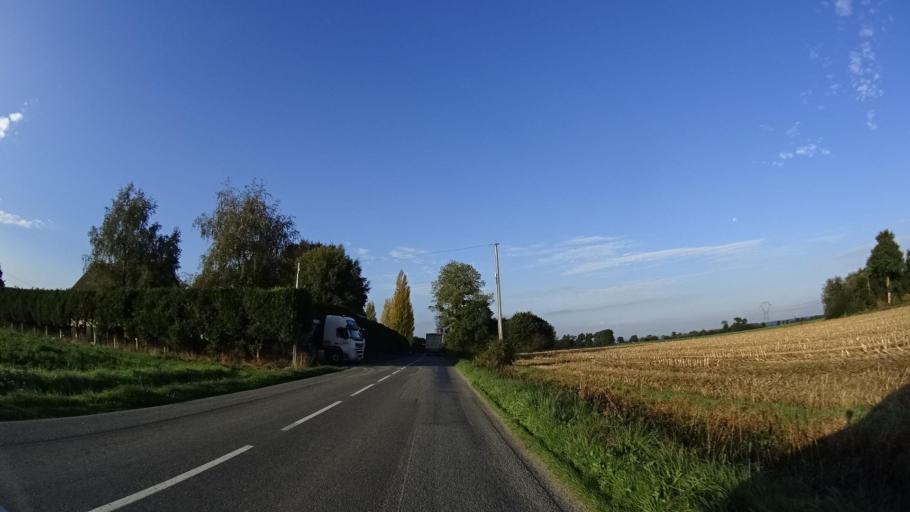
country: FR
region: Brittany
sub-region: Departement d'Ille-et-Vilaine
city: Quedillac
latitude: 48.2554
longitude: -2.1179
